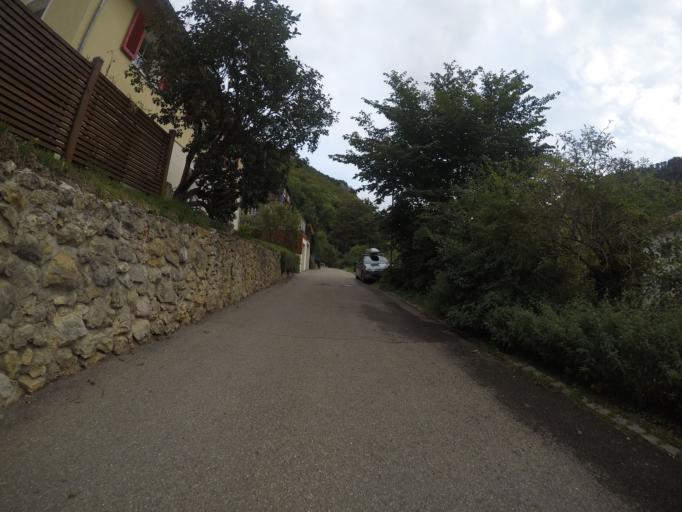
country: DE
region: Baden-Wuerttemberg
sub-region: Tuebingen Region
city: Pfullingen
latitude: 48.4130
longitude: 9.2624
